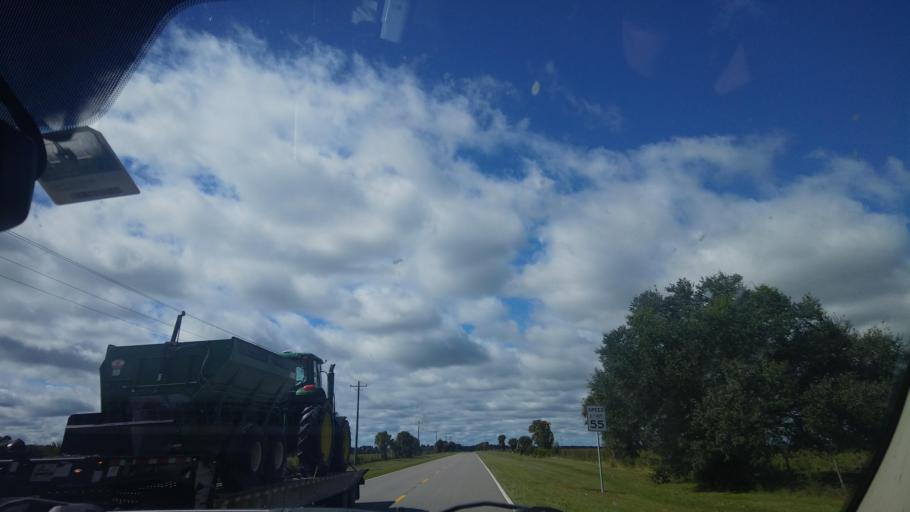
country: US
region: Florida
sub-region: Okeechobee County
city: Okeechobee
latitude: 27.3945
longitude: -80.8966
